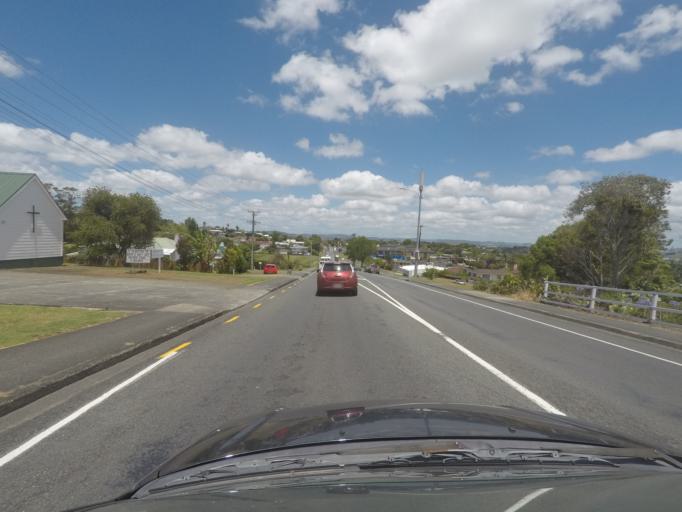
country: NZ
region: Northland
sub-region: Whangarei
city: Whangarei
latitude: -35.7517
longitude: 174.3680
